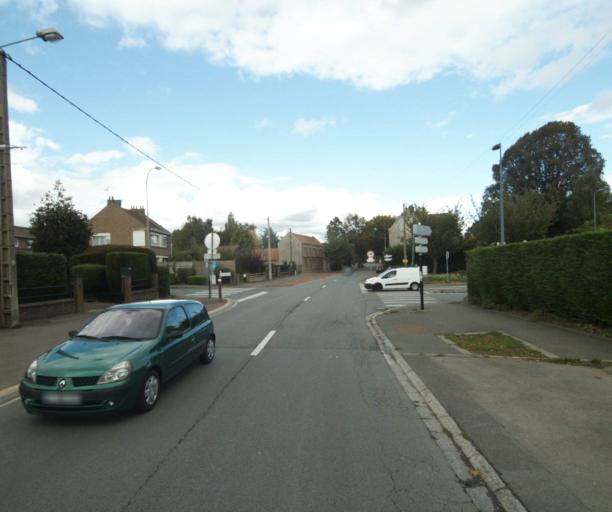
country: FR
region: Nord-Pas-de-Calais
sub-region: Departement du Nord
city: Capinghem
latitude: 50.6412
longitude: 2.9720
